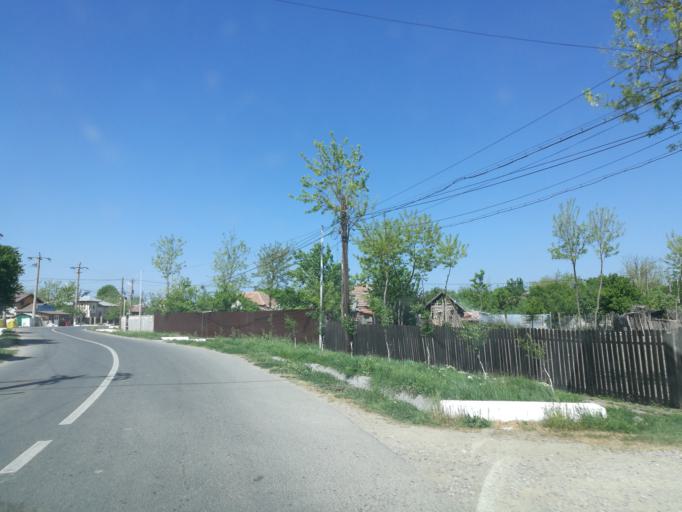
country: RO
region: Ialomita
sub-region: Comuna Adancata
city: Adancata
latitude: 44.7646
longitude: 26.4405
